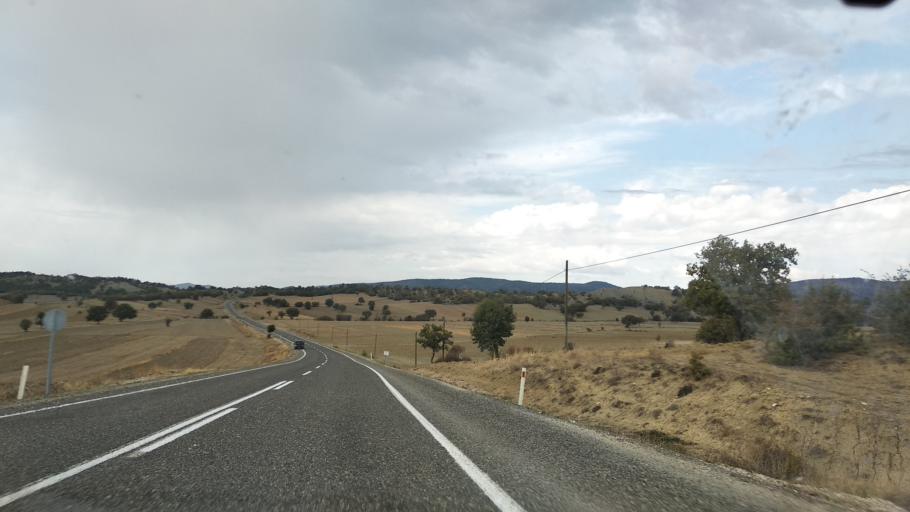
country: TR
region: Bolu
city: Seben
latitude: 40.3328
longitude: 31.4563
